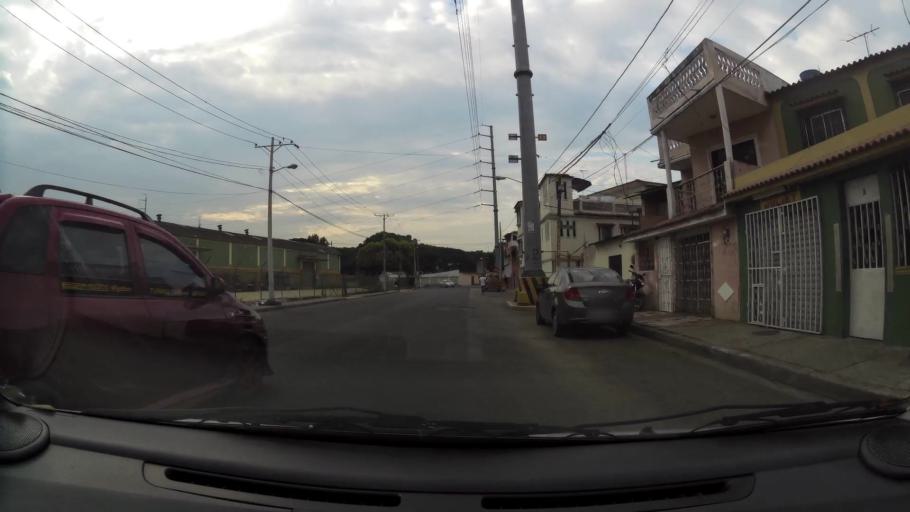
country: EC
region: Guayas
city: Guayaquil
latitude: -2.2425
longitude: -79.8841
